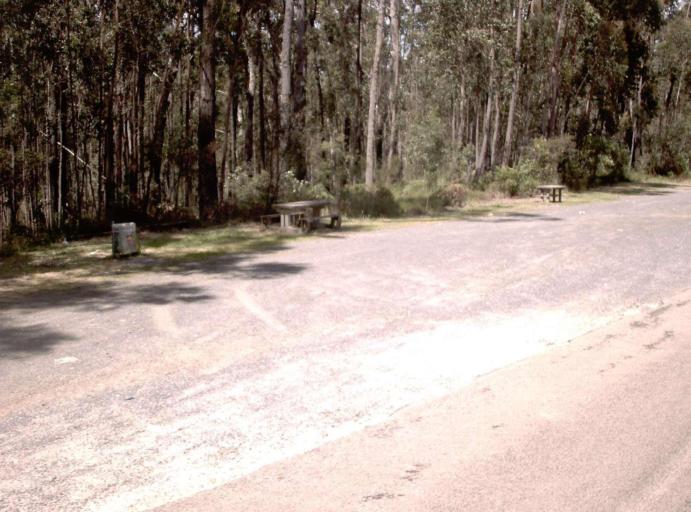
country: AU
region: New South Wales
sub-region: Bombala
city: Bombala
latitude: -37.5750
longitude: 149.3055
